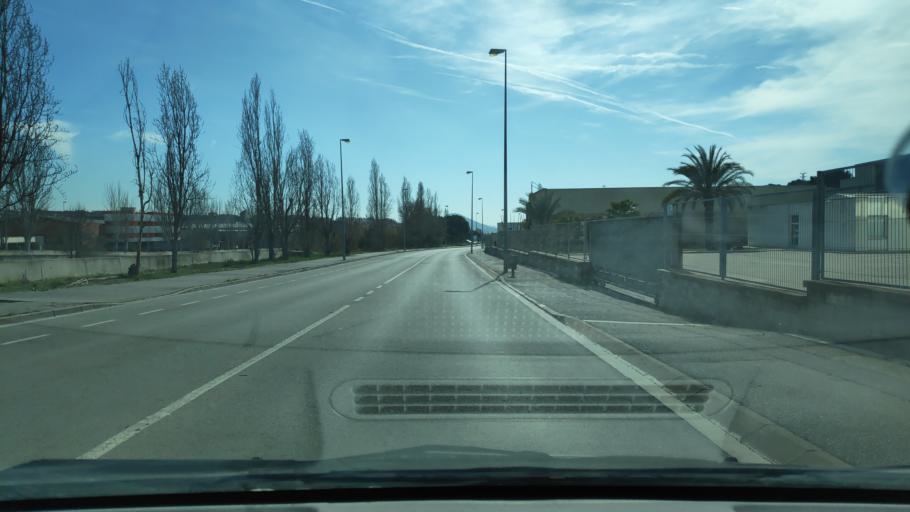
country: ES
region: Catalonia
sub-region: Provincia de Barcelona
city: Rubi
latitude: 41.5099
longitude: 2.0333
